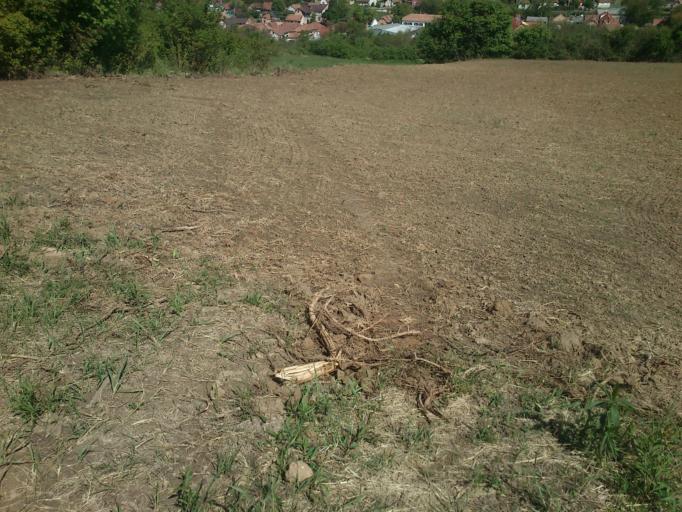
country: HU
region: Komarom-Esztergom
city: Kesztolc
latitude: 47.7089
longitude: 18.7985
